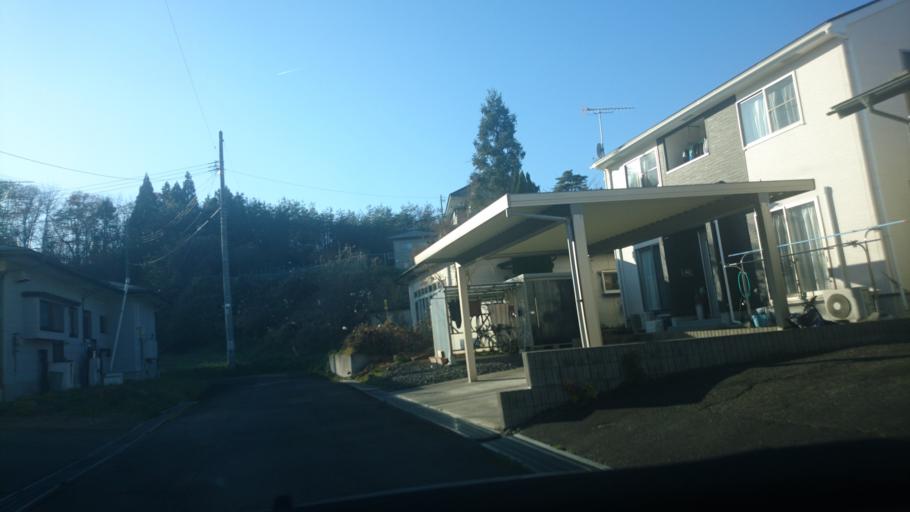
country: JP
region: Iwate
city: Ichinoseki
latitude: 38.9067
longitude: 141.1878
